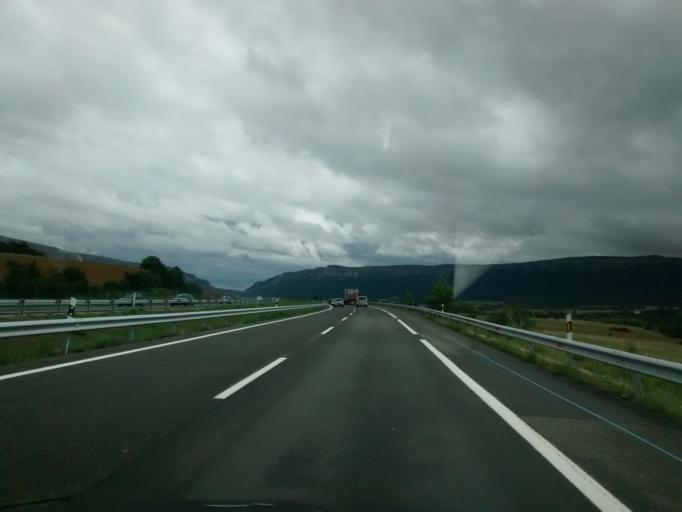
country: ES
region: Basque Country
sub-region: Provincia de Alava
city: Murguia
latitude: 42.9024
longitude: -2.8970
